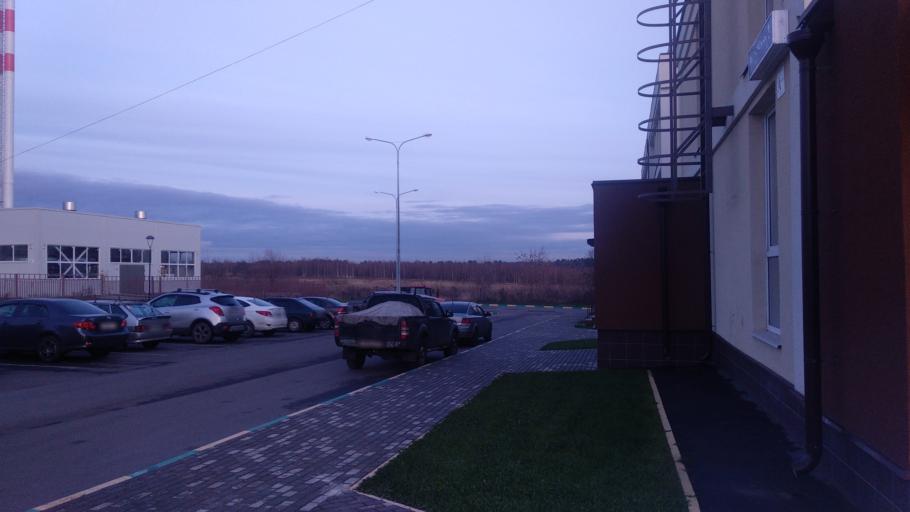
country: RU
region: Moskovskaya
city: Nakhabino
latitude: 55.8571
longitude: 37.1851
